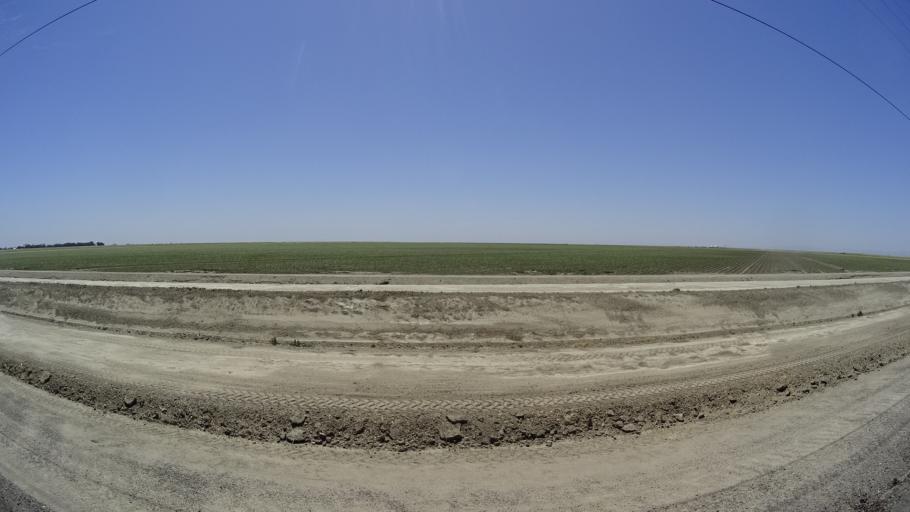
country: US
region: California
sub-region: Kings County
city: Corcoran
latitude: 36.1091
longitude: -119.6128
